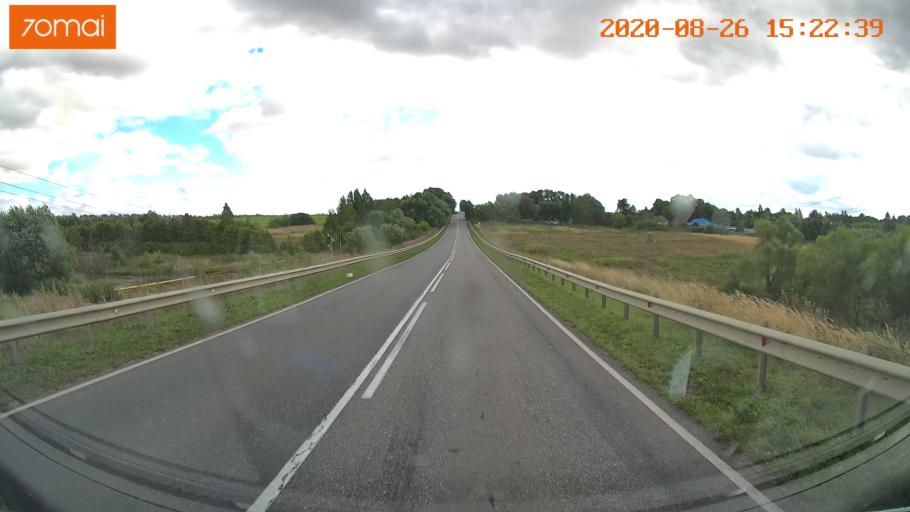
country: RU
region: Tula
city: Severo-Zadonsk
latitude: 54.1279
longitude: 38.4551
